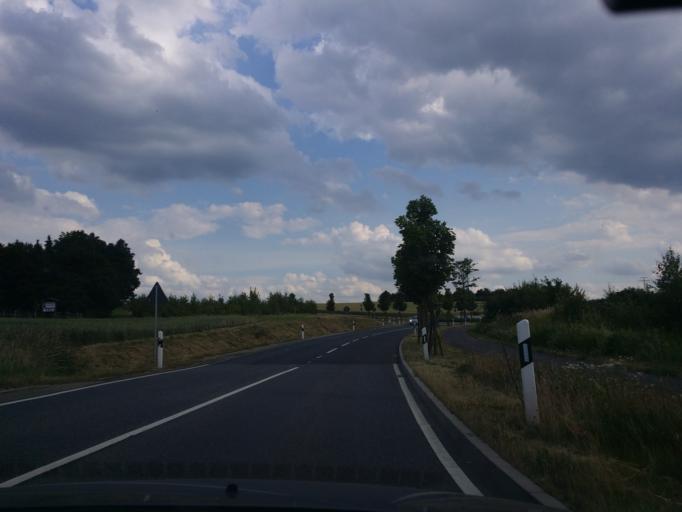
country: DE
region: Hesse
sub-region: Regierungsbezirk Darmstadt
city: Idstein
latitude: 50.2097
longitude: 8.2788
